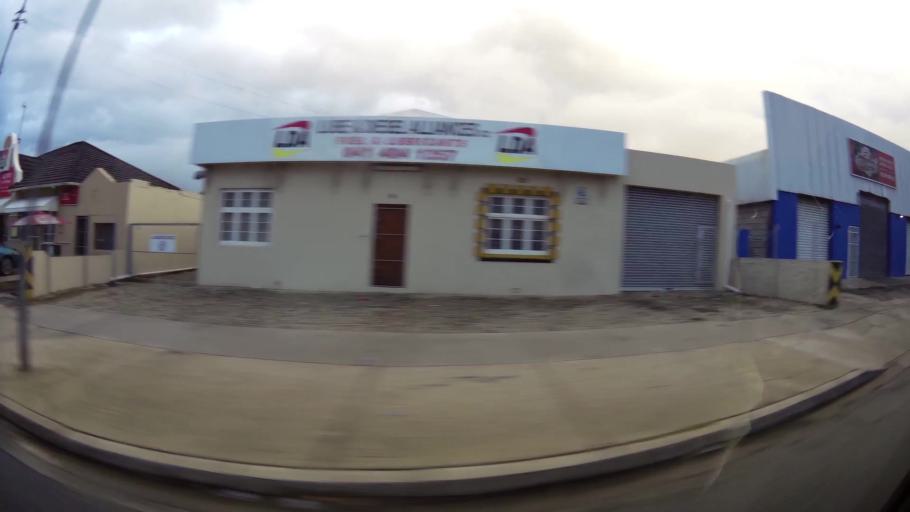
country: ZA
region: Eastern Cape
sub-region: Nelson Mandela Bay Metropolitan Municipality
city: Port Elizabeth
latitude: -33.9268
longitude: 25.5995
